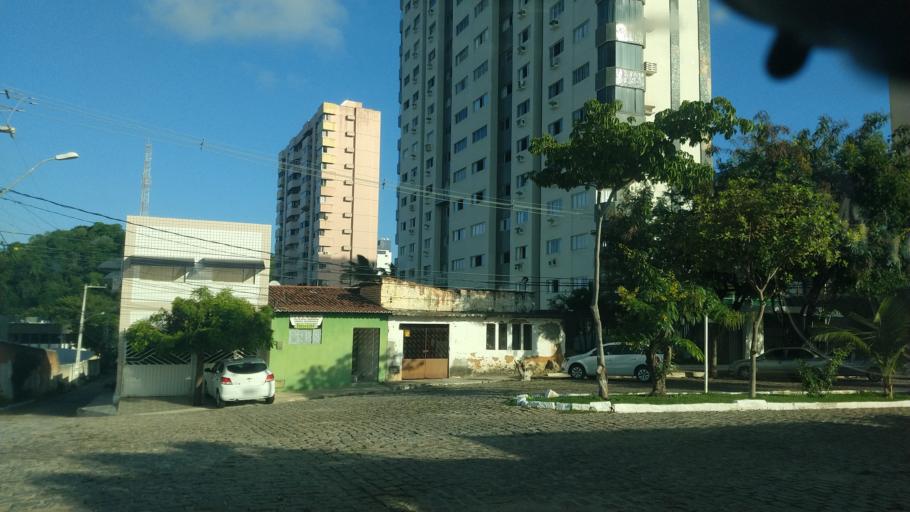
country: BR
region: Rio Grande do Norte
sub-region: Natal
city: Natal
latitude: -5.8123
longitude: -35.1988
